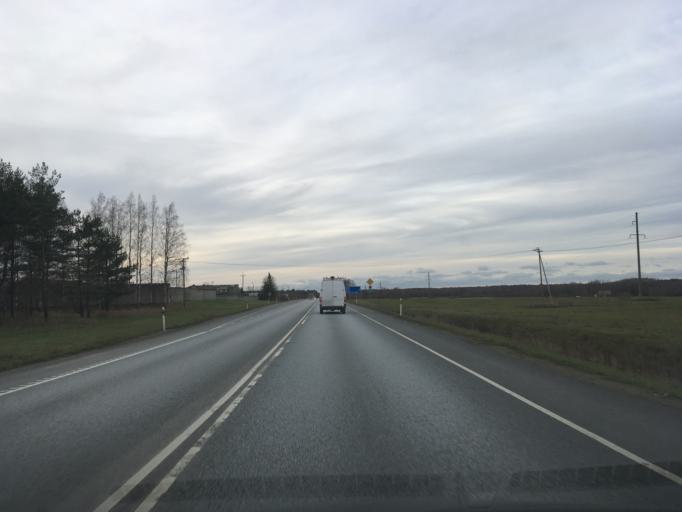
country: EE
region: Ida-Virumaa
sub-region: Kohtla-Jaerve linn
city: Kohtla-Jarve
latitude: 59.4085
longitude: 27.3167
